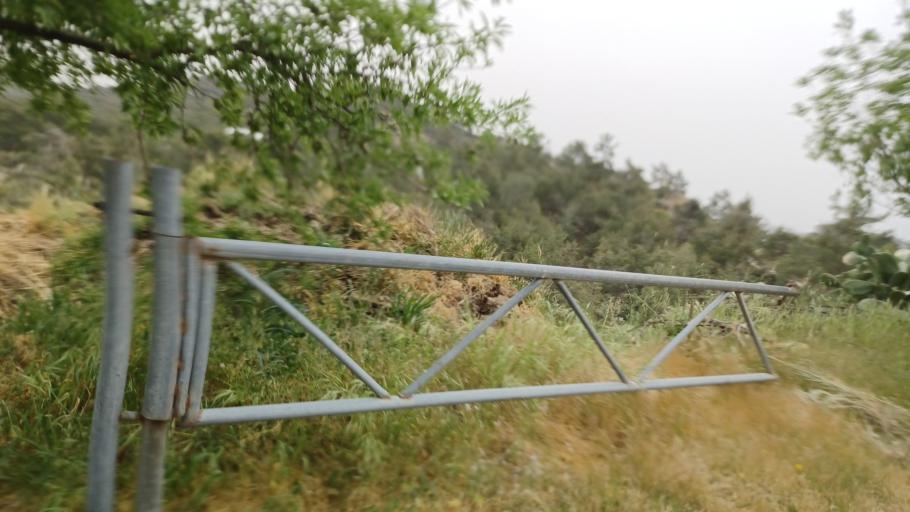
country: CY
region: Limassol
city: Parekklisha
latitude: 34.8598
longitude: 33.0956
